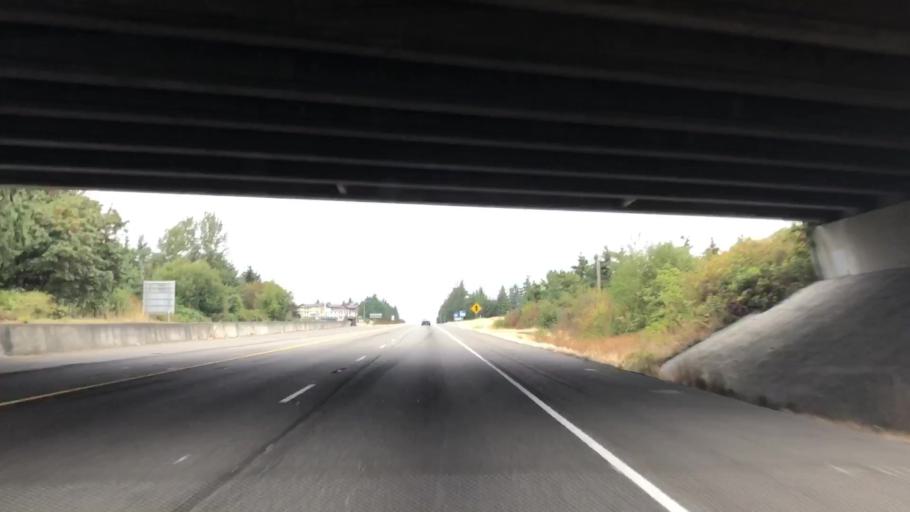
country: US
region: Washington
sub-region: Pierce County
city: Gig Harbor
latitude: 47.3053
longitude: -122.5762
